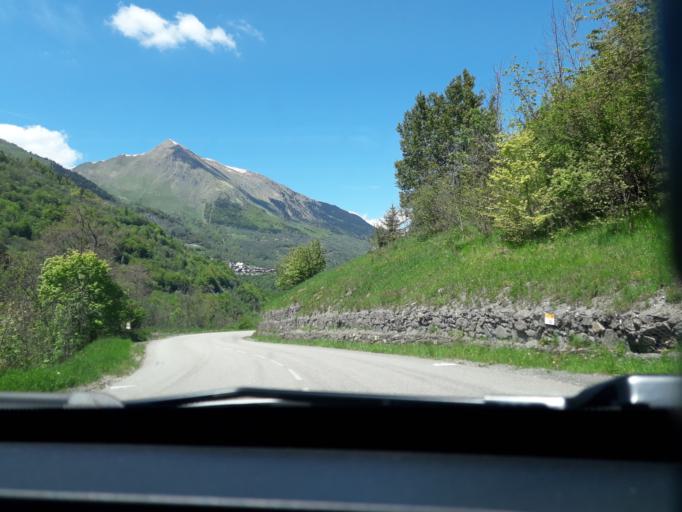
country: FR
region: Rhone-Alpes
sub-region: Departement de la Savoie
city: Saint-Martin-de-Belleville
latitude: 45.4072
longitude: 6.4912
